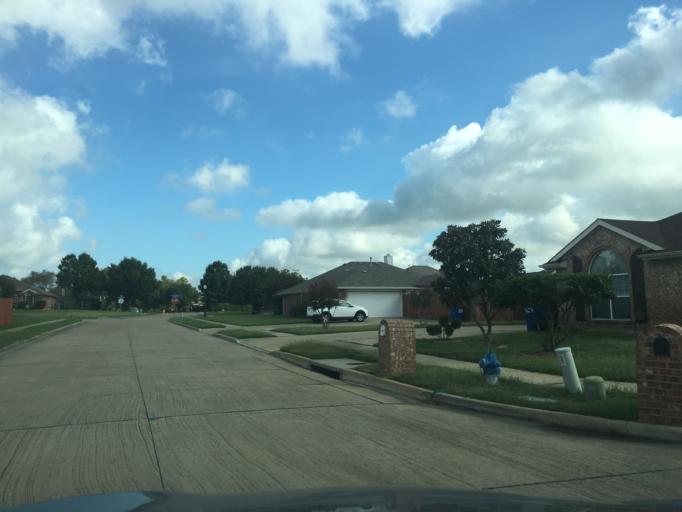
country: US
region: Texas
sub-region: Dallas County
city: Sachse
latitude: 32.9659
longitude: -96.5887
